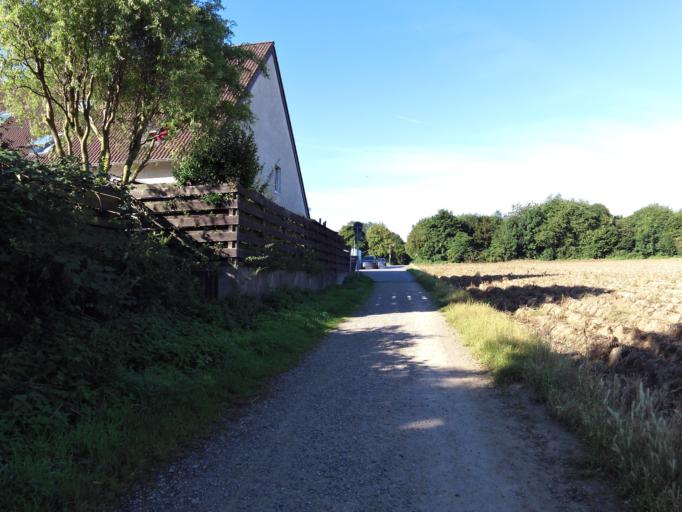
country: DE
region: North Rhine-Westphalia
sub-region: Regierungsbezirk Koln
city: Alsdorf
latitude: 50.8805
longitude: 6.1764
